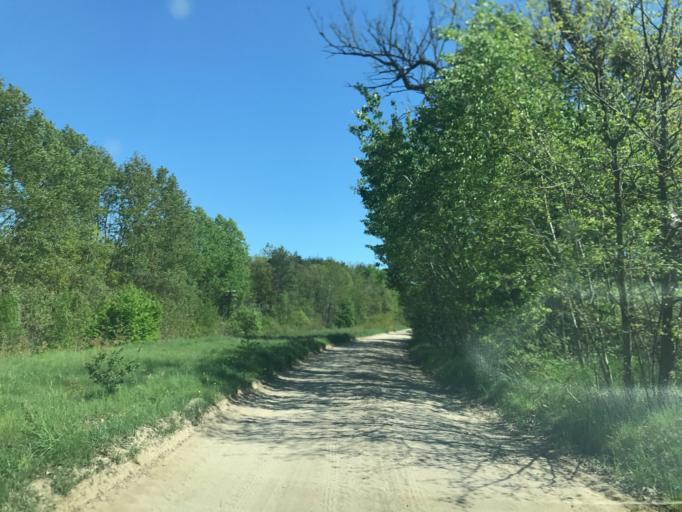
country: PL
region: Warmian-Masurian Voivodeship
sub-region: Powiat dzialdowski
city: Lidzbark
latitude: 53.2411
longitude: 19.7694
